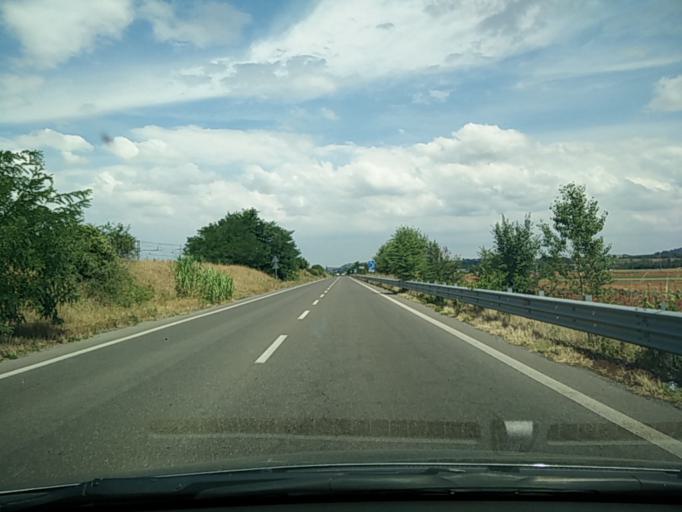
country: IT
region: Lombardy
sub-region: Provincia di Pavia
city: Montebello
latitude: 45.0089
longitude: 9.0958
